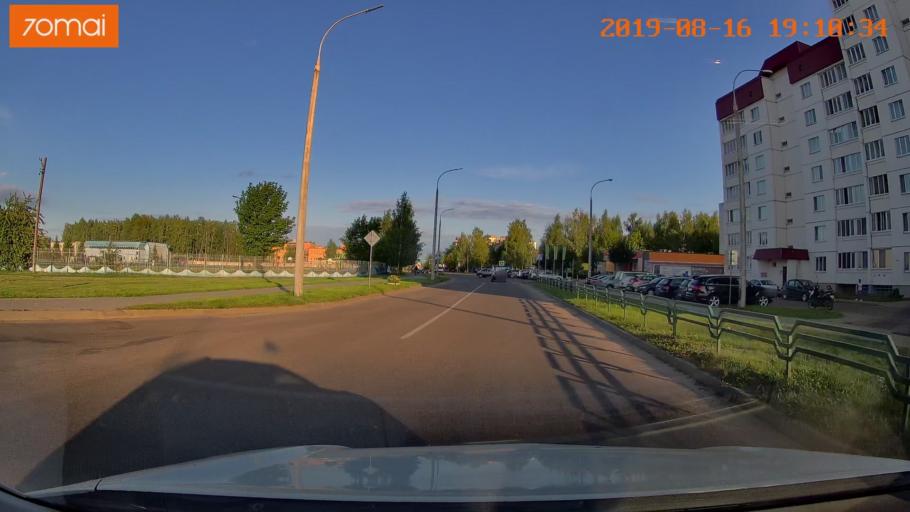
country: BY
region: Mogilev
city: Asipovichy
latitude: 53.3235
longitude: 28.6422
